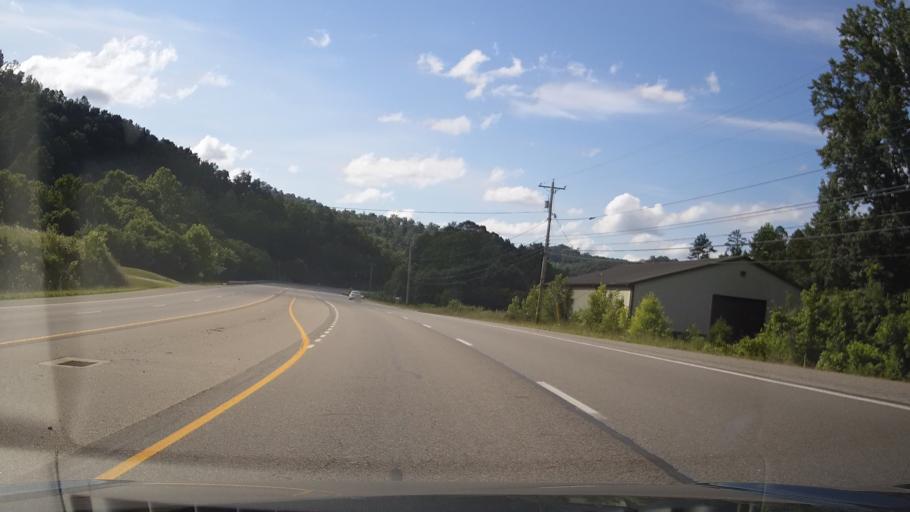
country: US
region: Kentucky
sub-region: Martin County
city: Inez
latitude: 37.9609
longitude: -82.6678
